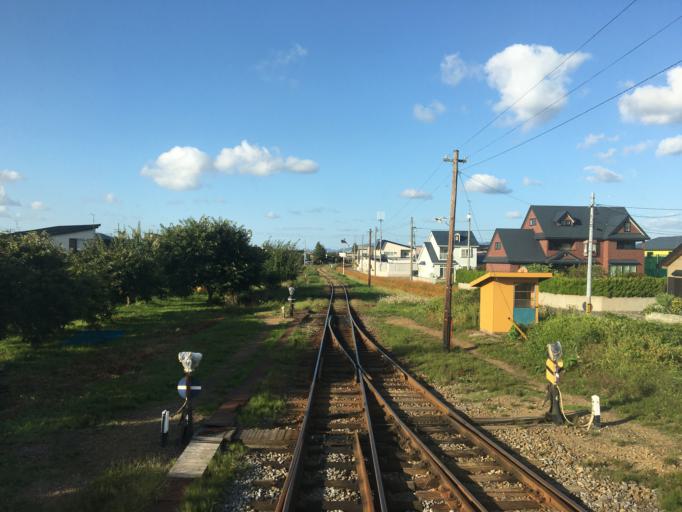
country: JP
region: Aomori
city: Goshogawara
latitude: 40.8111
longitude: 140.4490
